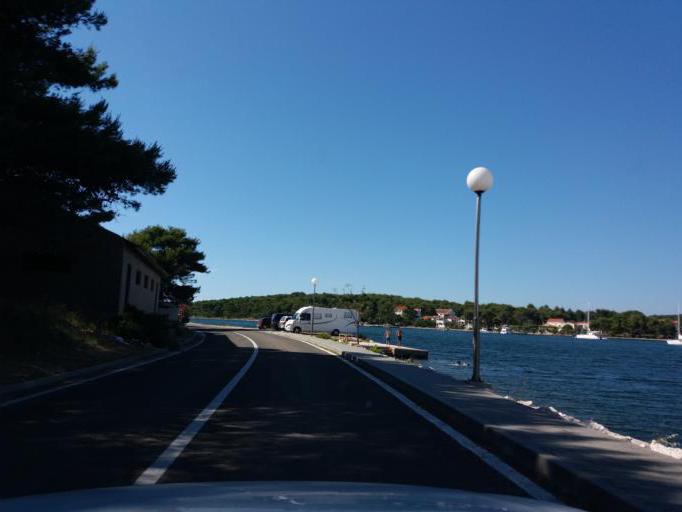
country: HR
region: Zadarska
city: Ugljan
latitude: 44.1393
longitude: 14.8551
